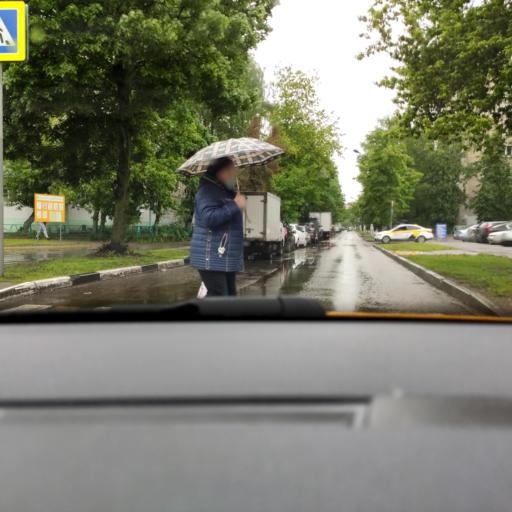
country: RU
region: Moskovskaya
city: Balashikha
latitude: 55.7937
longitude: 37.9704
